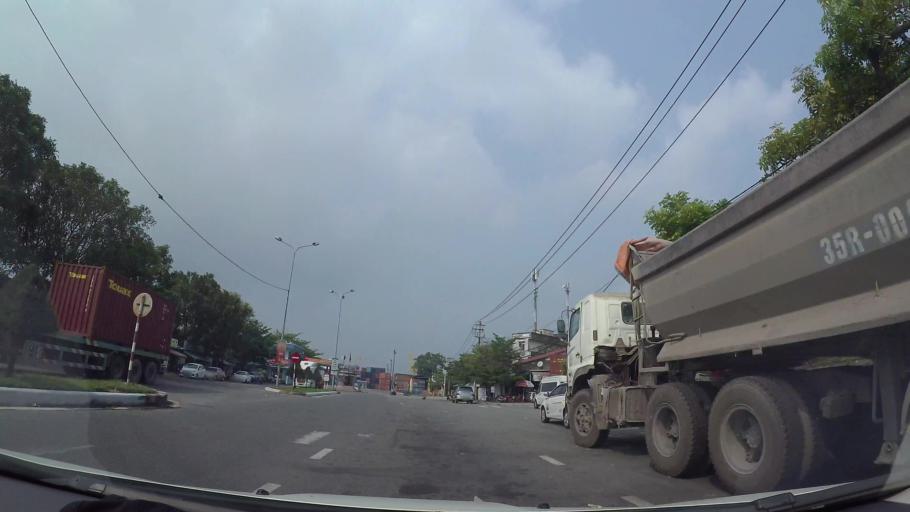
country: VN
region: Da Nang
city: Da Nang
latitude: 16.1223
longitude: 108.2200
